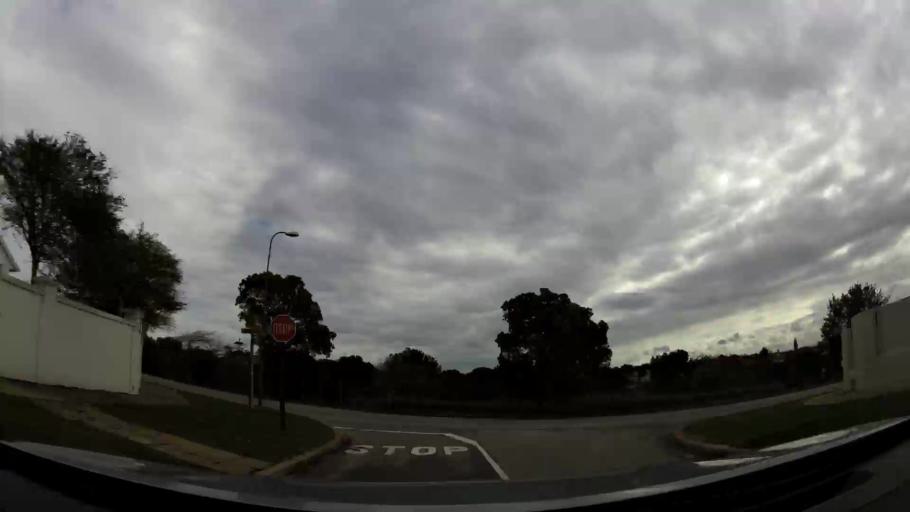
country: ZA
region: Eastern Cape
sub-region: Nelson Mandela Bay Metropolitan Municipality
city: Port Elizabeth
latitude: -33.9507
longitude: 25.5937
